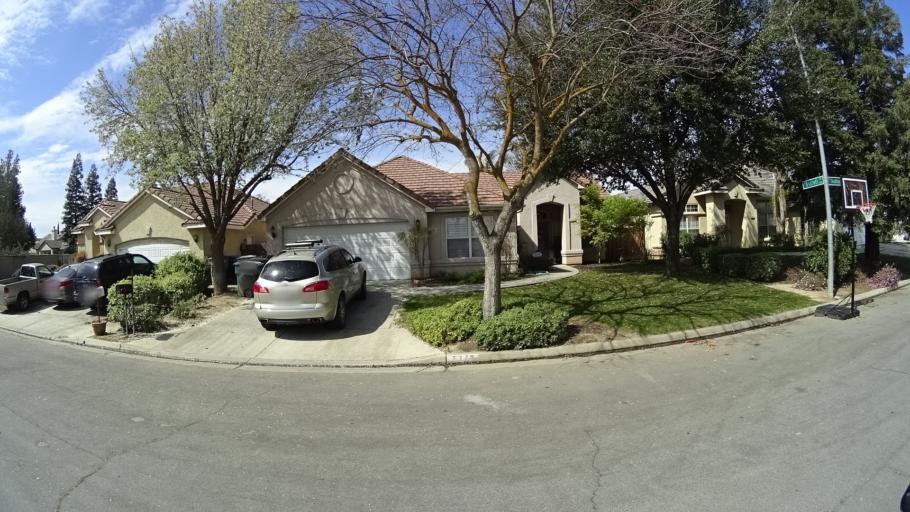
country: US
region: California
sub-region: Fresno County
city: Biola
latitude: 36.8484
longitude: -119.8921
